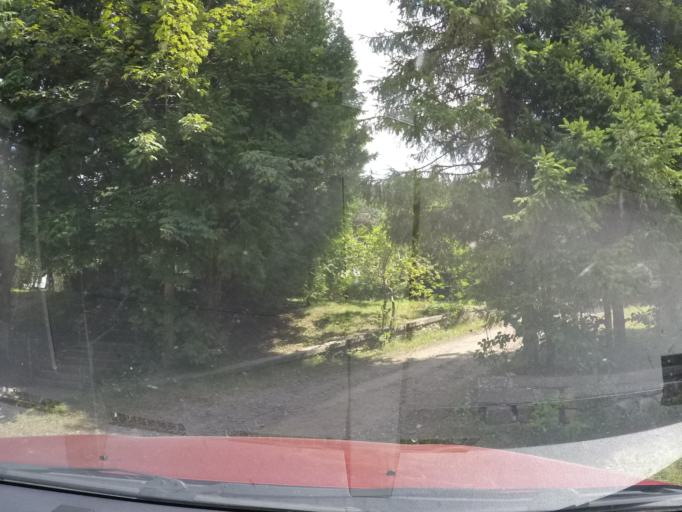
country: UA
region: Zakarpattia
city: Velykyi Bereznyi
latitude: 49.0417
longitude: 22.5814
